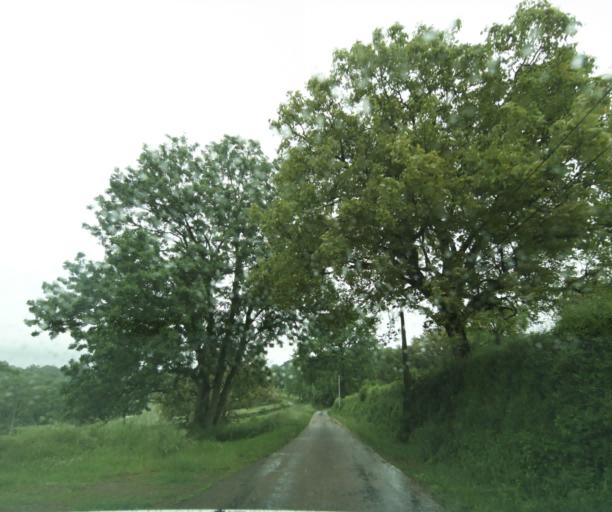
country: FR
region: Bourgogne
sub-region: Departement de Saone-et-Loire
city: Charolles
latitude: 46.4086
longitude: 4.3225
